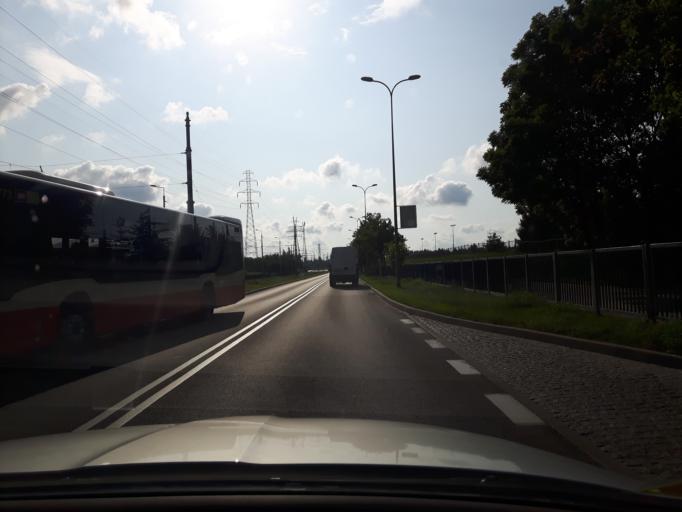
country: PL
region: Pomeranian Voivodeship
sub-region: Gdansk
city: Gdansk
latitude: 54.3384
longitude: 18.6097
